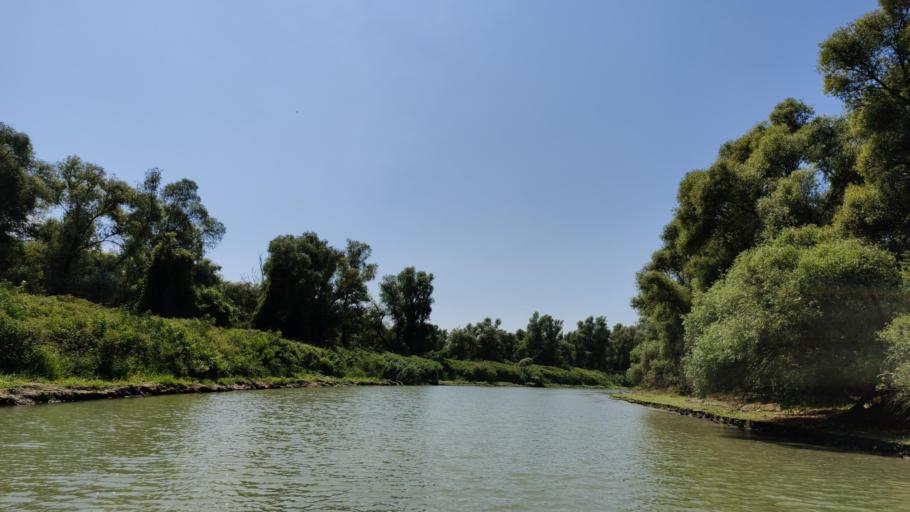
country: RO
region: Tulcea
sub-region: Comuna Pardina
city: Pardina
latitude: 45.2549
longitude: 28.9559
